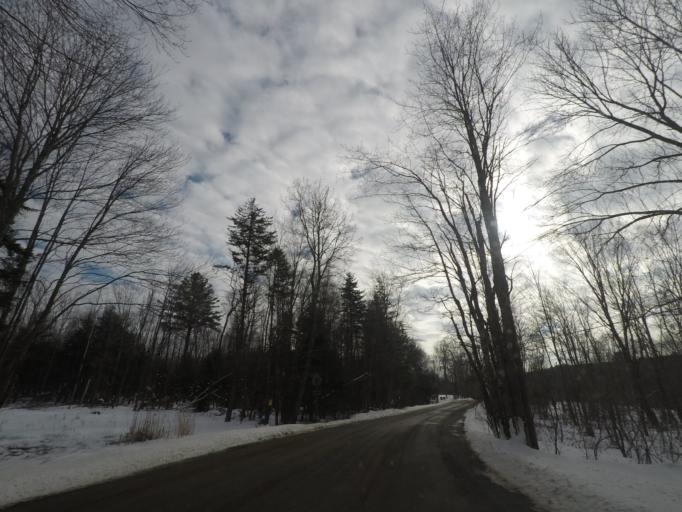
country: US
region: New York
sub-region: Rensselaer County
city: Averill Park
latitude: 42.6383
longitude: -73.4795
